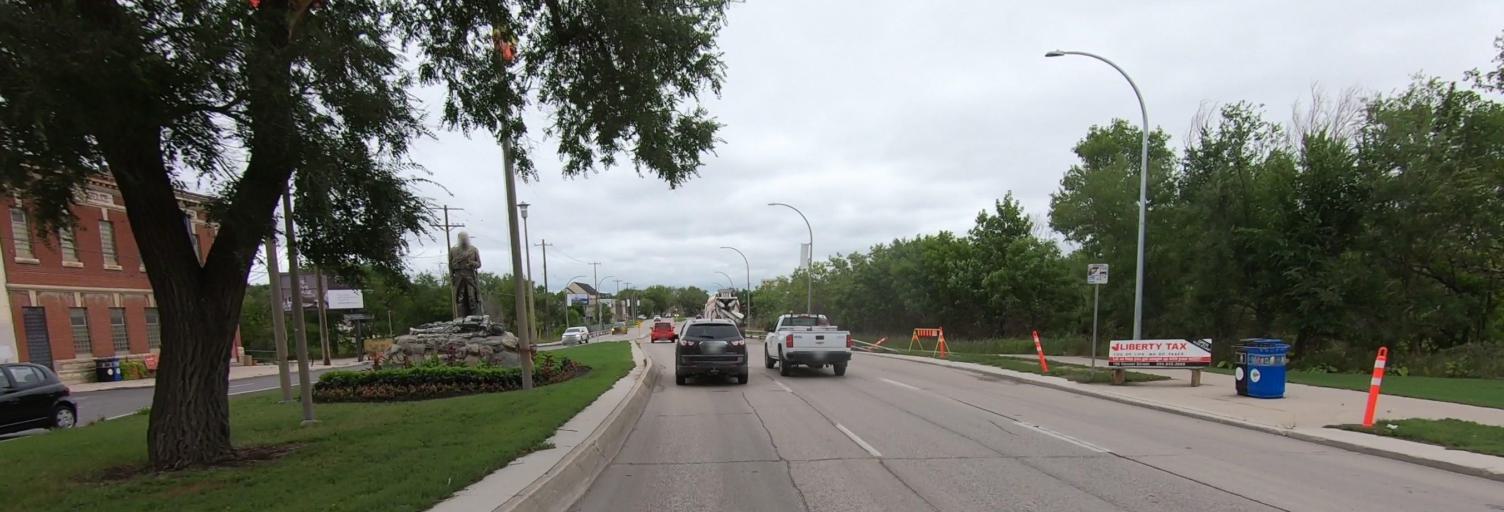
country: CA
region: Manitoba
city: Winnipeg
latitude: 49.8948
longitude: -97.1115
